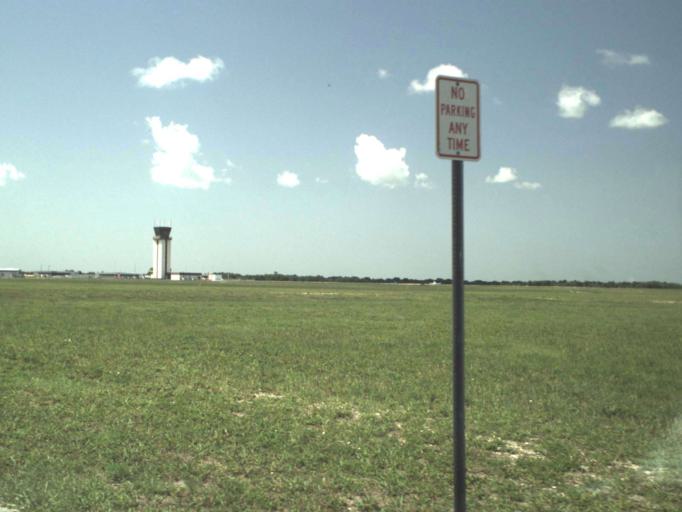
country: US
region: Florida
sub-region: Seminole County
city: Midway
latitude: 28.7706
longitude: -81.2381
